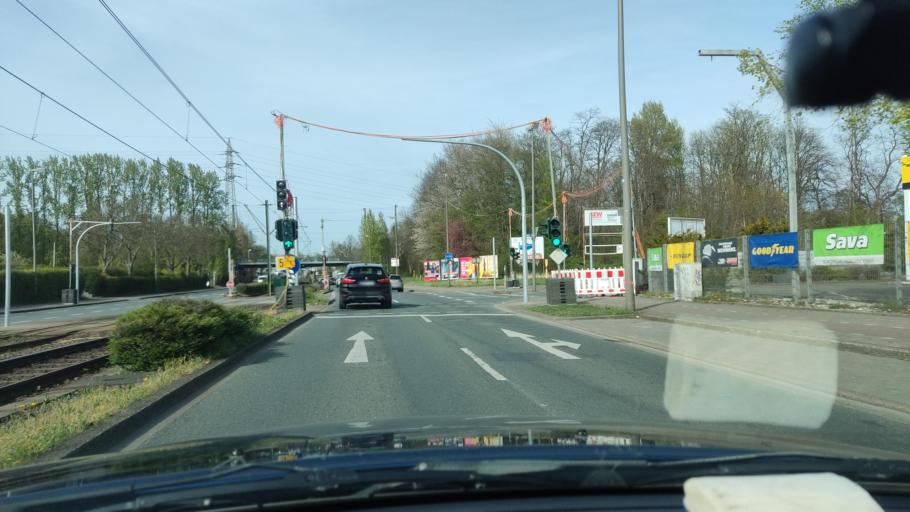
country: DE
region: North Rhine-Westphalia
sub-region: Regierungsbezirk Arnsberg
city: Dortmund
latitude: 51.5380
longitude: 7.4756
